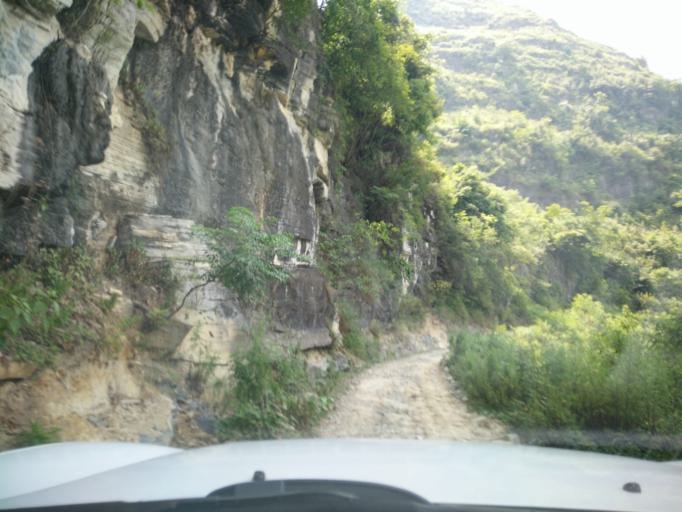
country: CN
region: Guangxi Zhuangzu Zizhiqu
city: Xinzhou
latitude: 25.0199
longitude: 105.7056
